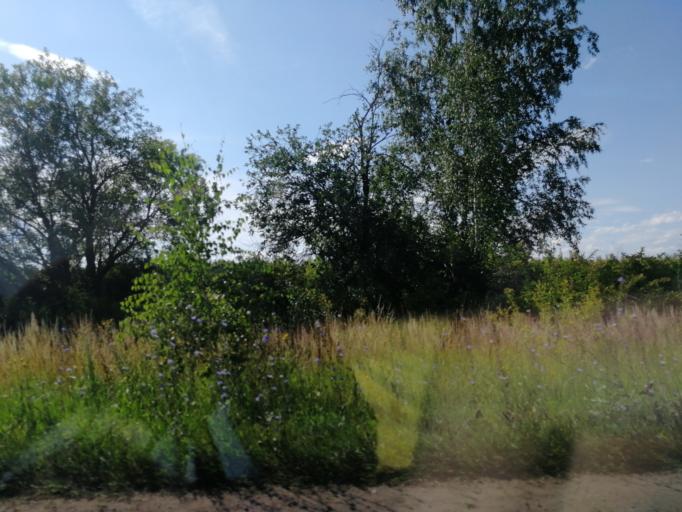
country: RU
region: Tula
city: Tovarkovskiy
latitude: 53.6366
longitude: 38.2500
